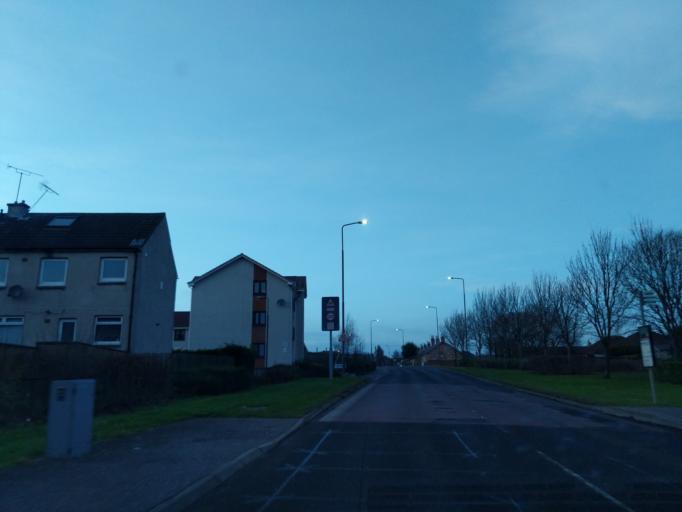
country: GB
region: Scotland
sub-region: Midlothian
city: Bonnyrigg
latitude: 55.8706
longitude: -3.0953
